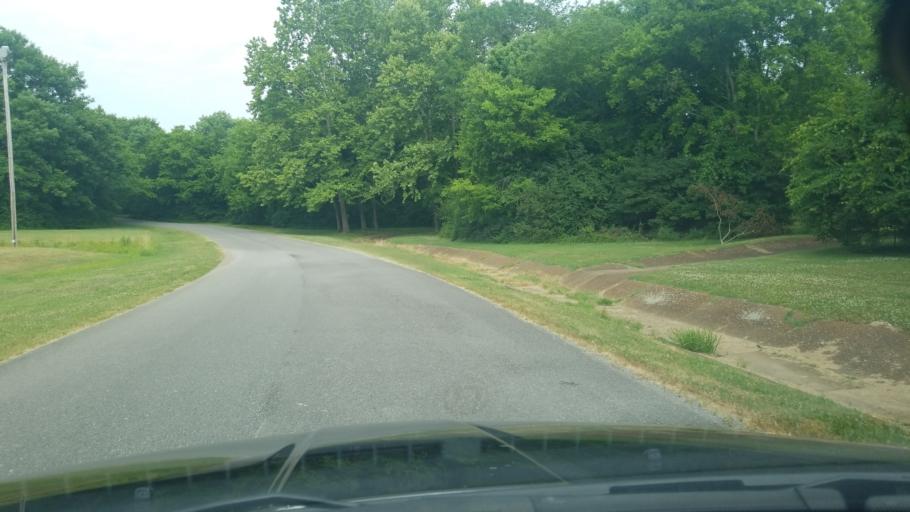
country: US
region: Tennessee
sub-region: Davidson County
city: Goodlettsville
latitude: 36.2753
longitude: -86.7454
